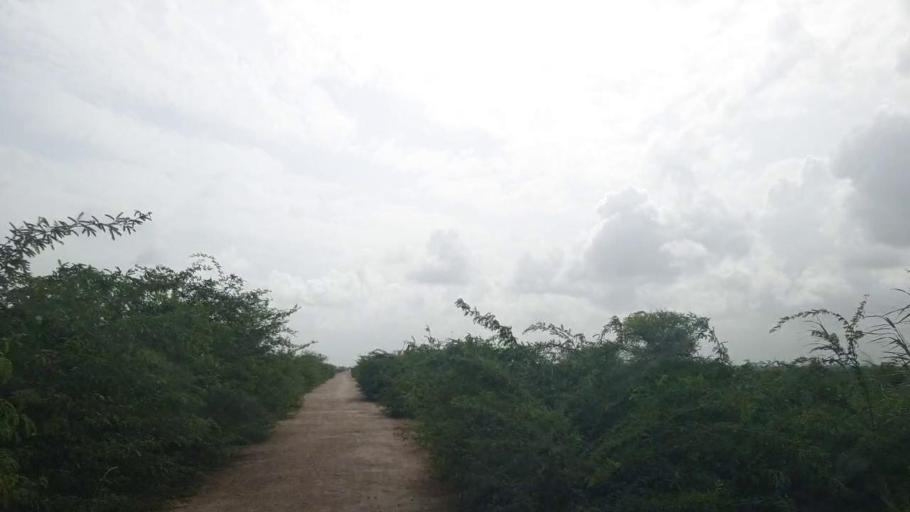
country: PK
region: Sindh
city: Tando Bago
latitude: 24.8224
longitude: 69.0600
